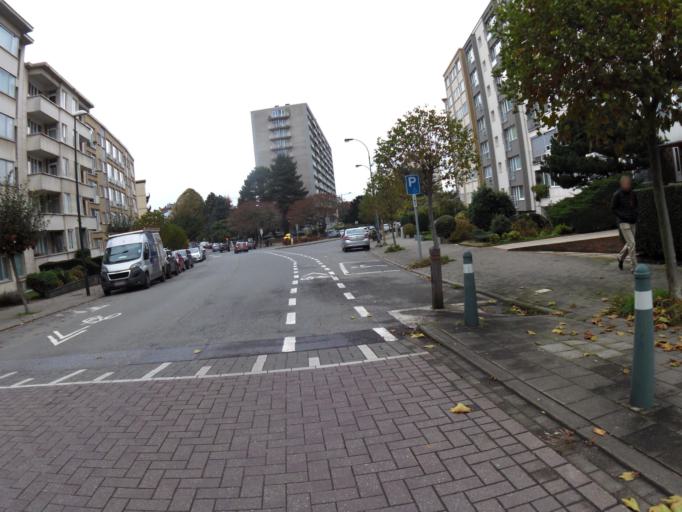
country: BE
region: Brussels Capital
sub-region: Bruxelles-Capitale
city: Brussels
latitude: 50.8225
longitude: 4.4093
